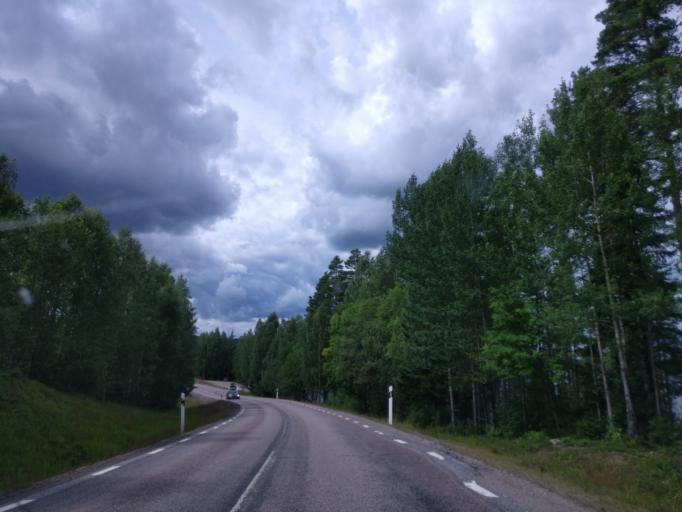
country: SE
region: Vaermland
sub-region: Hagfors Kommun
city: Ekshaerad
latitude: 60.1866
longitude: 13.3358
